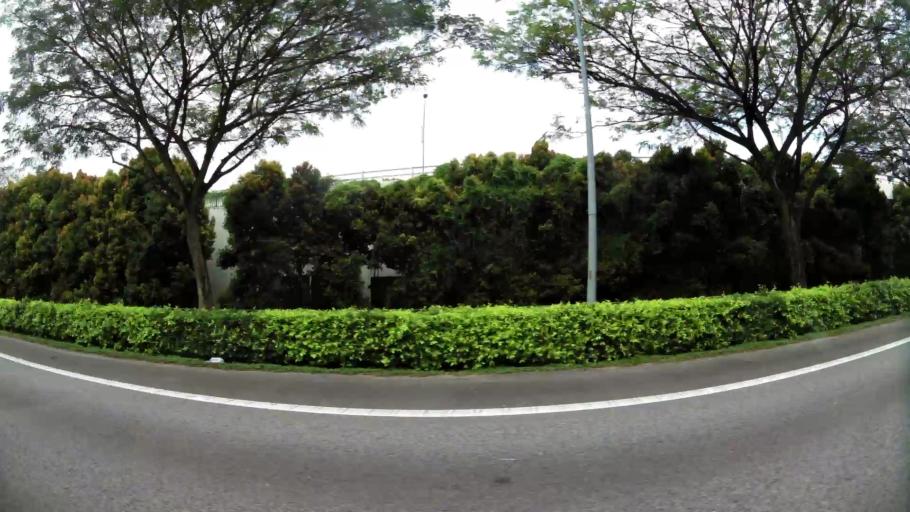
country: SG
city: Singapore
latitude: 1.3701
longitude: 103.9078
